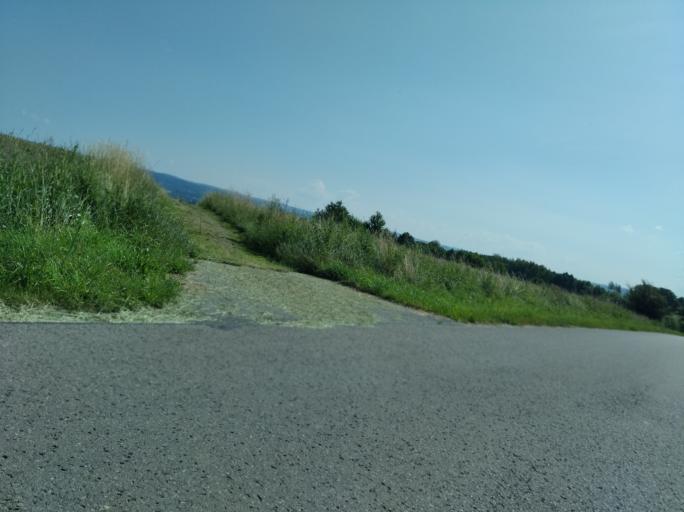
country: PL
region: Subcarpathian Voivodeship
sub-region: Powiat rzeszowski
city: Dynow
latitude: 49.8132
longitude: 22.2076
